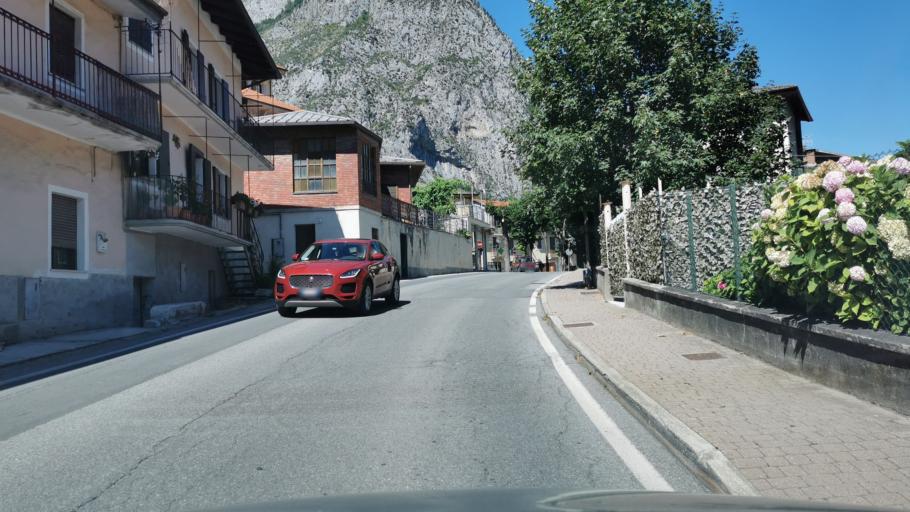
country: IT
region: Piedmont
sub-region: Provincia di Cuneo
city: Valdieri
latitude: 44.2763
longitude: 7.3972
